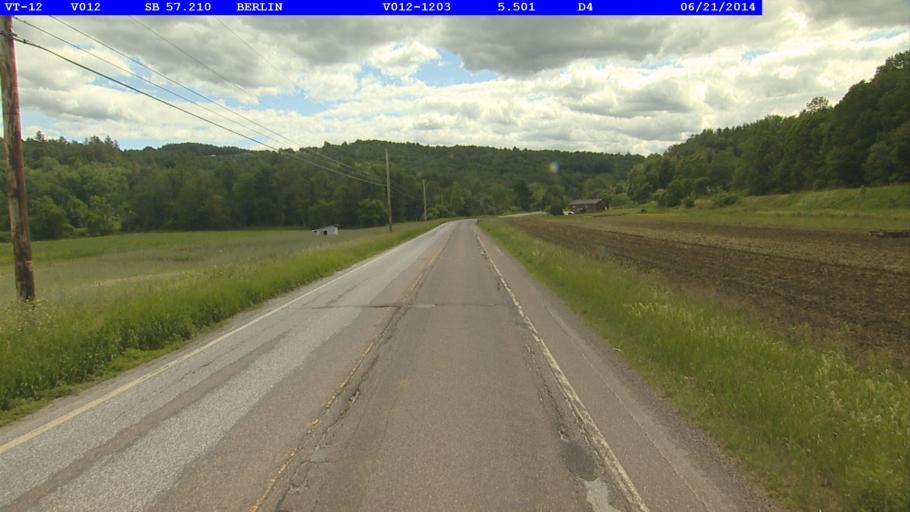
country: US
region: Vermont
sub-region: Washington County
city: Montpelier
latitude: 44.2328
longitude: -72.5995
